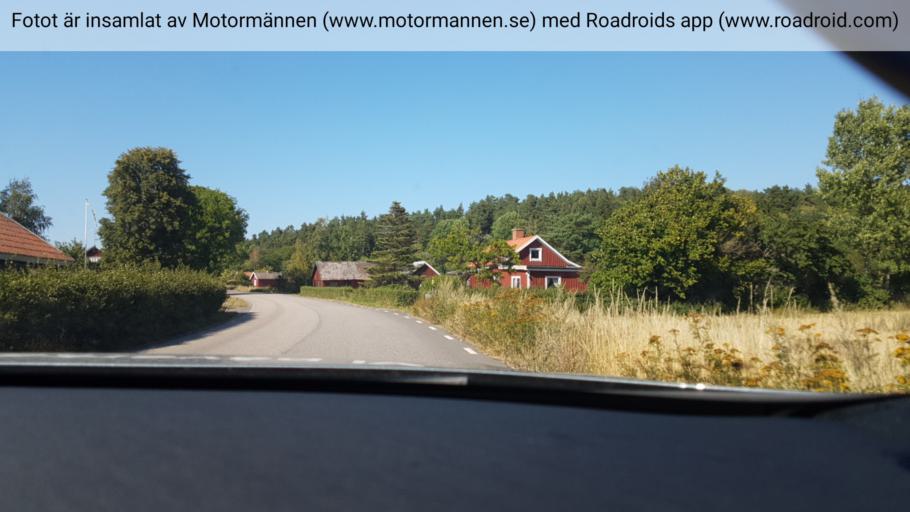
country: SE
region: Vaestra Goetaland
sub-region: Gotene Kommun
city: Kallby
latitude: 58.5209
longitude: 13.3219
